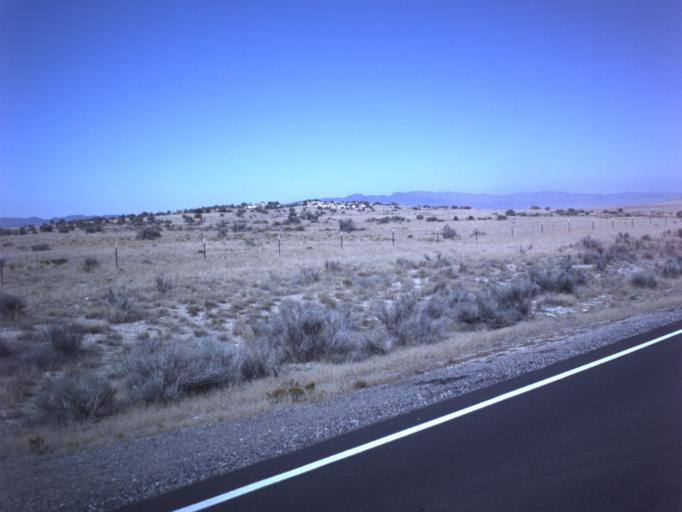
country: US
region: Utah
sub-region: Tooele County
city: Grantsville
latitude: 40.2889
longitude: -112.7422
